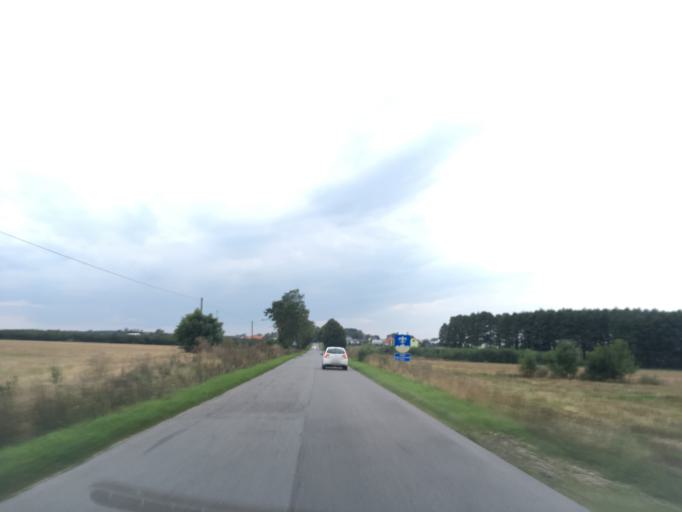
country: PL
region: Lodz Voivodeship
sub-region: Powiat piotrkowski
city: Leki Szlacheckie
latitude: 51.1889
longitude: 19.8196
